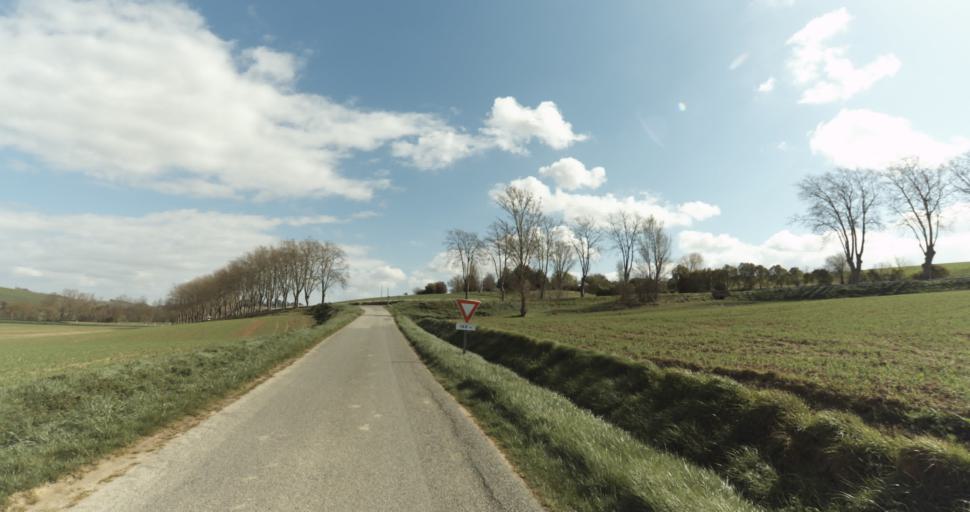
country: FR
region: Midi-Pyrenees
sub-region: Departement de la Haute-Garonne
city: Auterive
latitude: 43.3639
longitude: 1.5273
